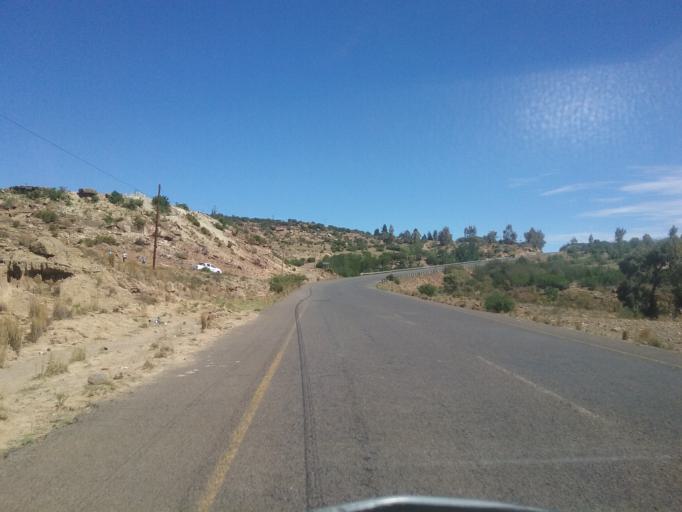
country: LS
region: Quthing
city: Quthing
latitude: -30.3679
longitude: 27.5522
